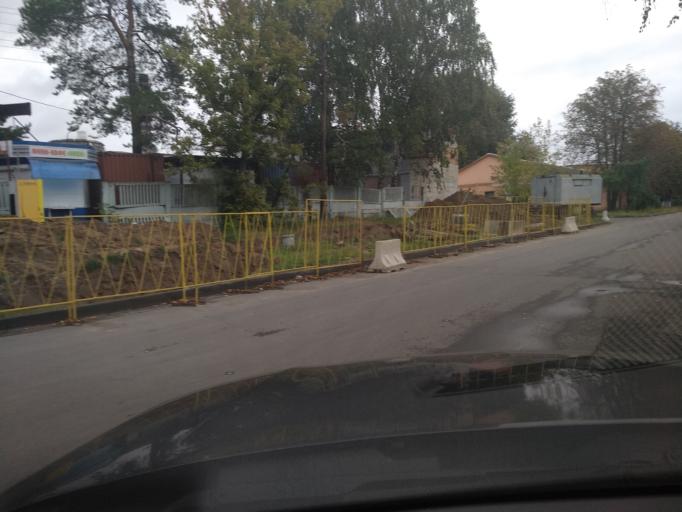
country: BY
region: Minsk
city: Minsk
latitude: 53.8772
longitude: 27.6405
